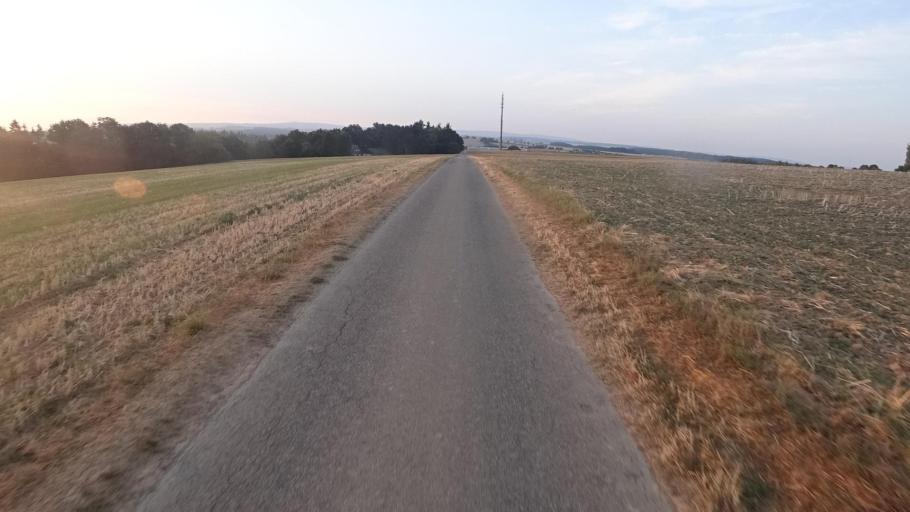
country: DE
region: Rheinland-Pfalz
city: Keidelheim
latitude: 49.9829
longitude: 7.5052
